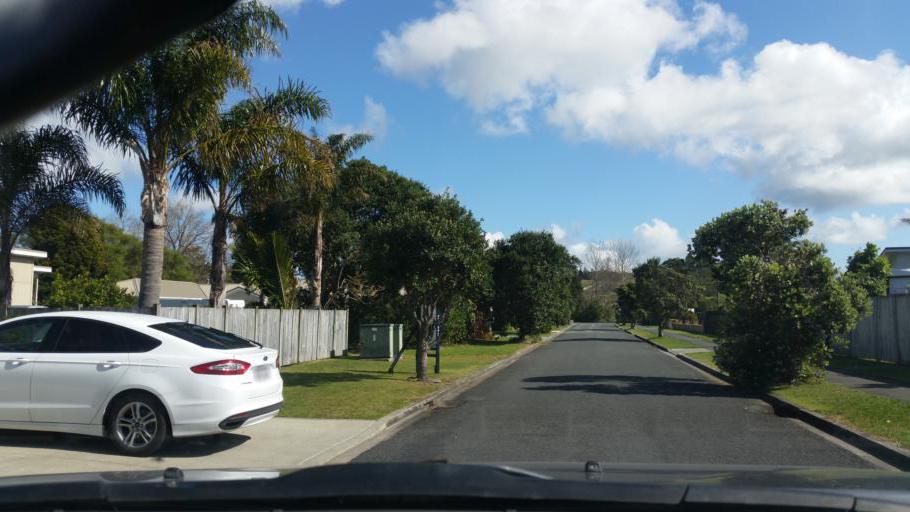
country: NZ
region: Auckland
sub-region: Auckland
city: Wellsford
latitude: -36.1282
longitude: 174.5717
